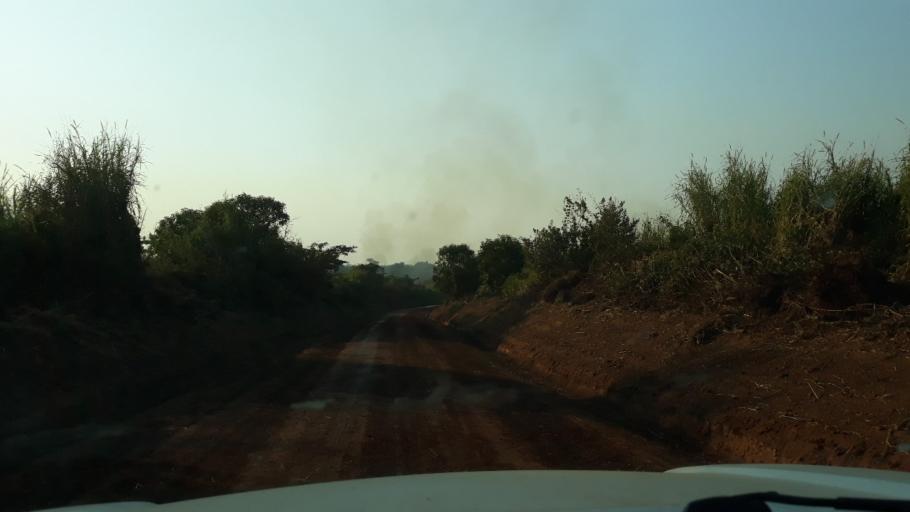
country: BI
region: Bururi
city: Rumonge
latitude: -4.2388
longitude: 28.9901
